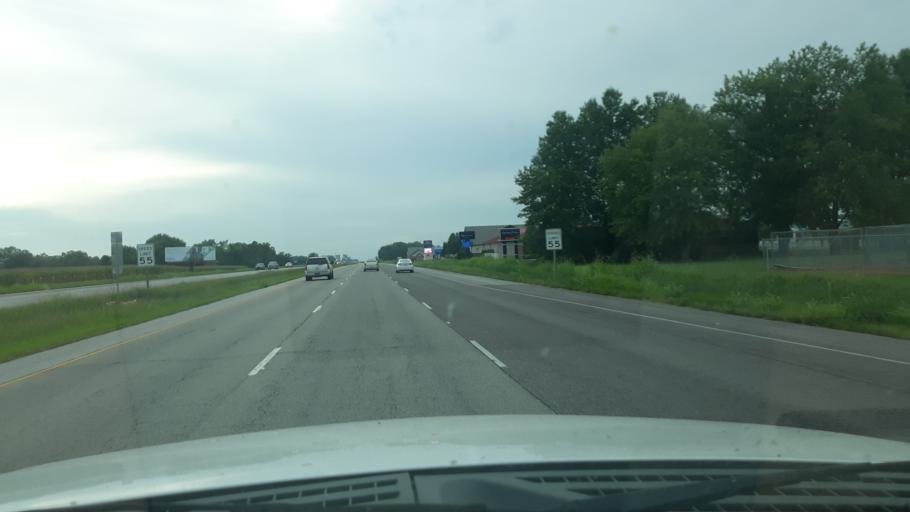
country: US
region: Illinois
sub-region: Williamson County
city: Energy
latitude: 37.7452
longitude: -89.0239
